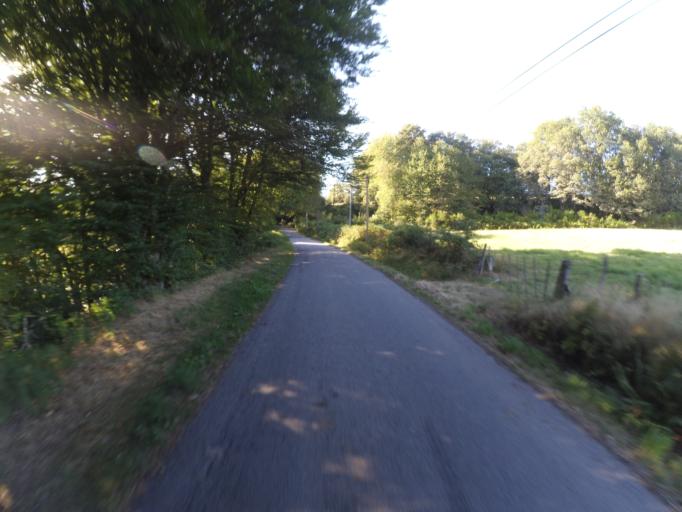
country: FR
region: Limousin
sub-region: Departement de la Creuse
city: Banize
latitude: 45.7696
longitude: 2.0168
